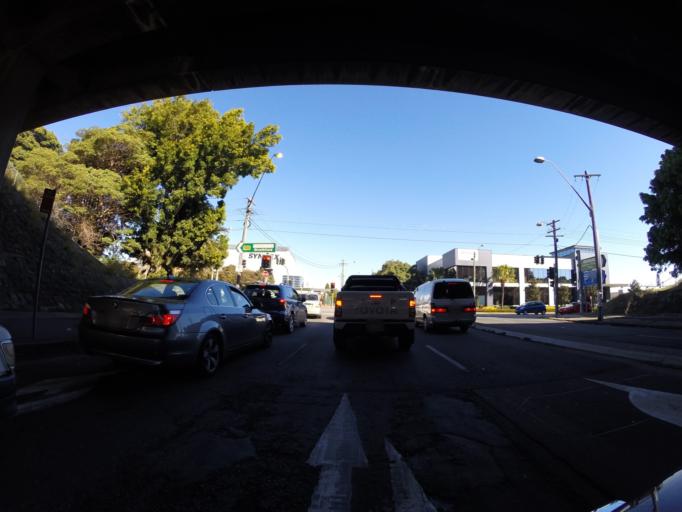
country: AU
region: New South Wales
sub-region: Auburn
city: Lidcombe
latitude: -33.8546
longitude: 151.0616
